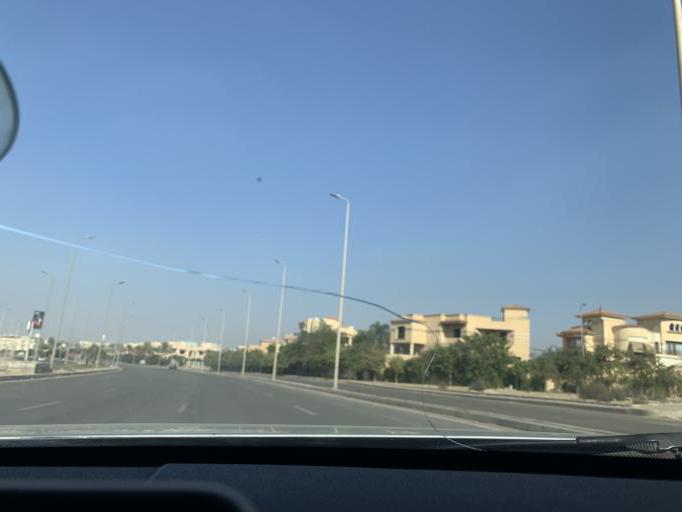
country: EG
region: Muhafazat al Qalyubiyah
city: Al Khankah
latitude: 30.0096
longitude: 31.4734
